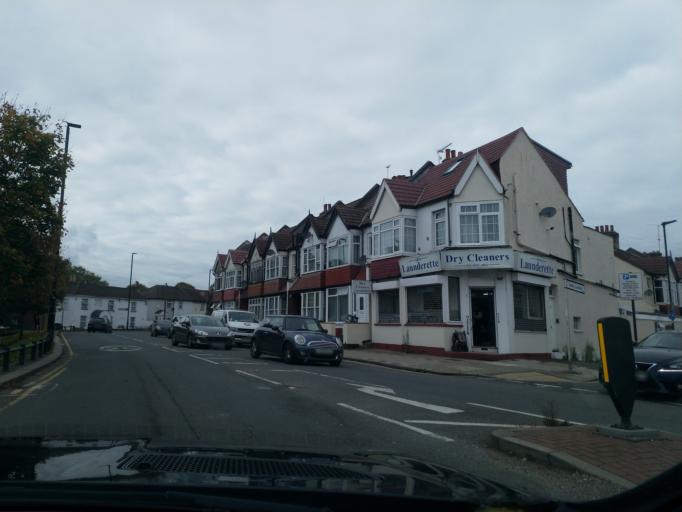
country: GB
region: England
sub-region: Greater London
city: Hounslow
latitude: 51.4774
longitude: -0.3610
